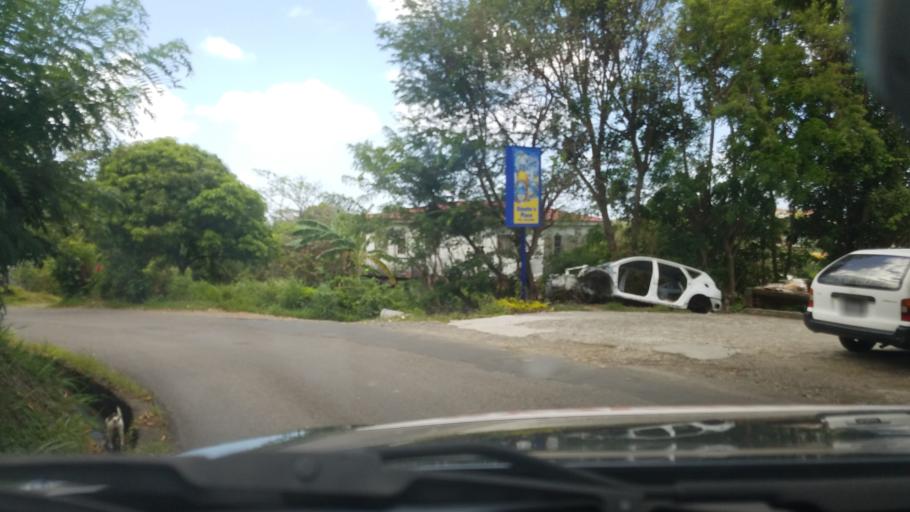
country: LC
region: Gros-Islet
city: Gros Islet
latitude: 14.0598
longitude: -60.9417
